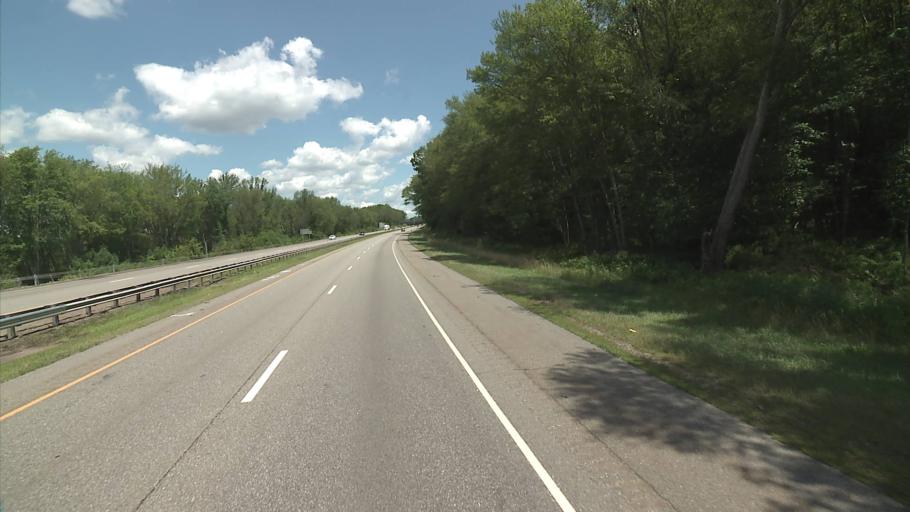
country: US
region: Connecticut
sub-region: Windham County
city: Moosup
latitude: 41.7301
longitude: -71.8884
